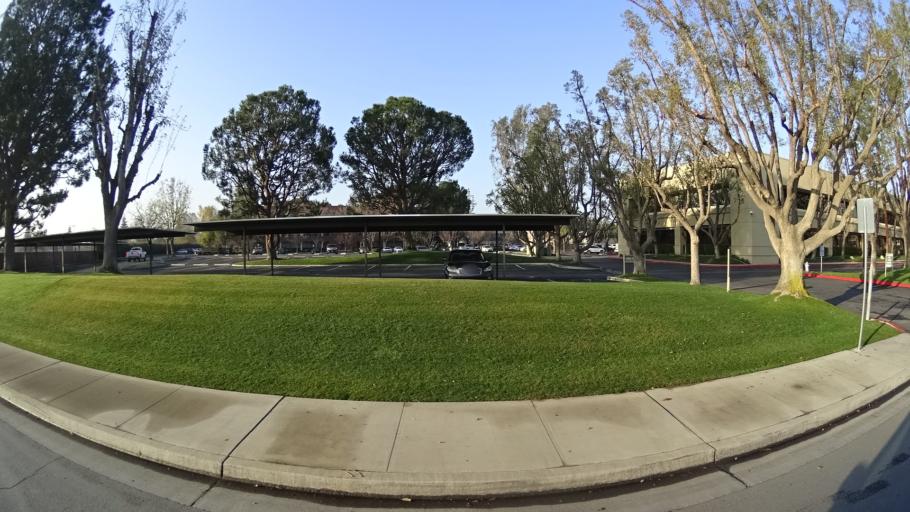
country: US
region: California
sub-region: Kern County
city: Bakersfield
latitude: 35.3628
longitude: -119.0562
